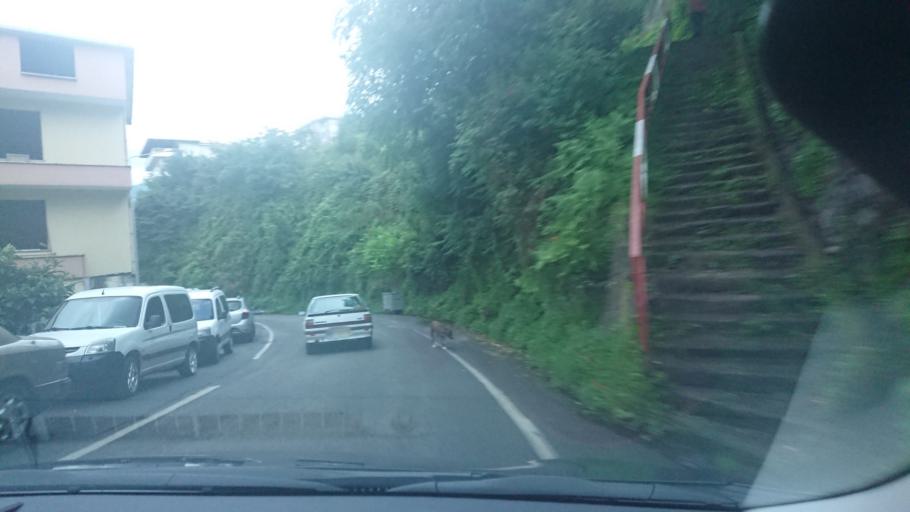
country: TR
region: Rize
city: Rize
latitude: 41.0273
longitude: 40.5116
